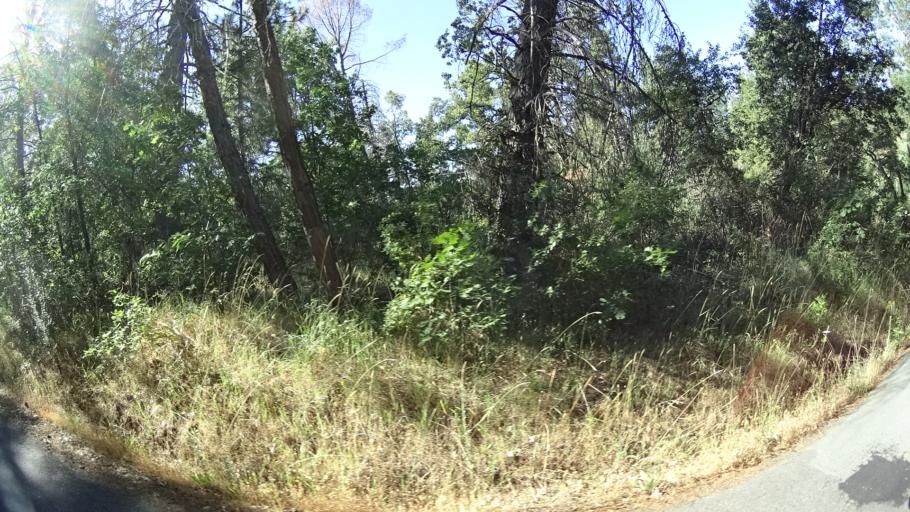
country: US
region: California
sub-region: Amador County
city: Pioneer
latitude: 38.4001
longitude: -120.5582
